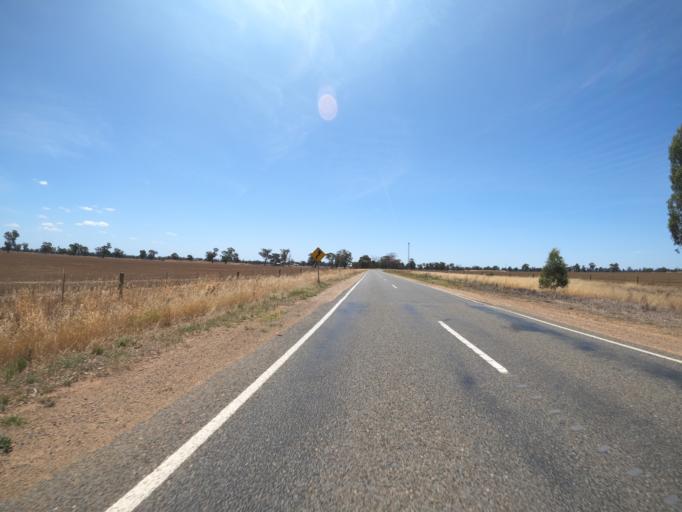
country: AU
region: Victoria
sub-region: Moira
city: Yarrawonga
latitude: -36.1930
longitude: 145.9670
